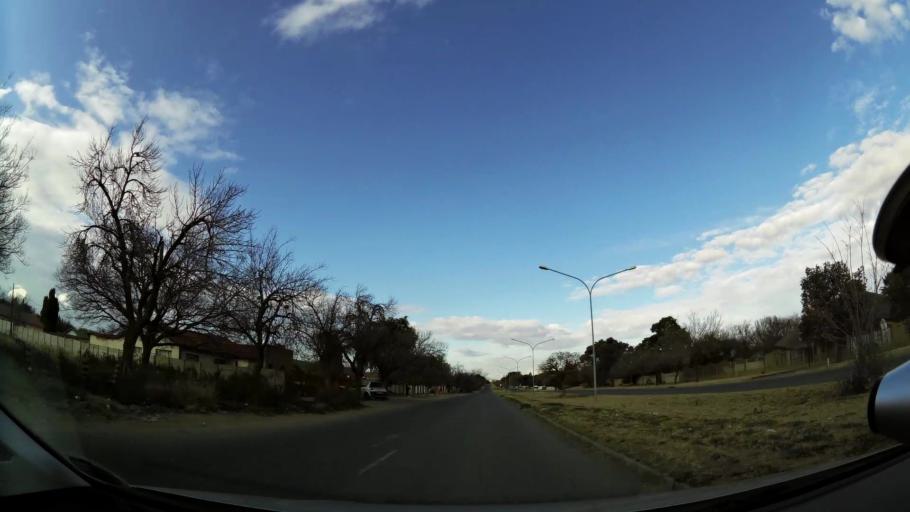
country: ZA
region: Orange Free State
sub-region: Lejweleputswa District Municipality
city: Welkom
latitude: -27.9812
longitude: 26.7037
